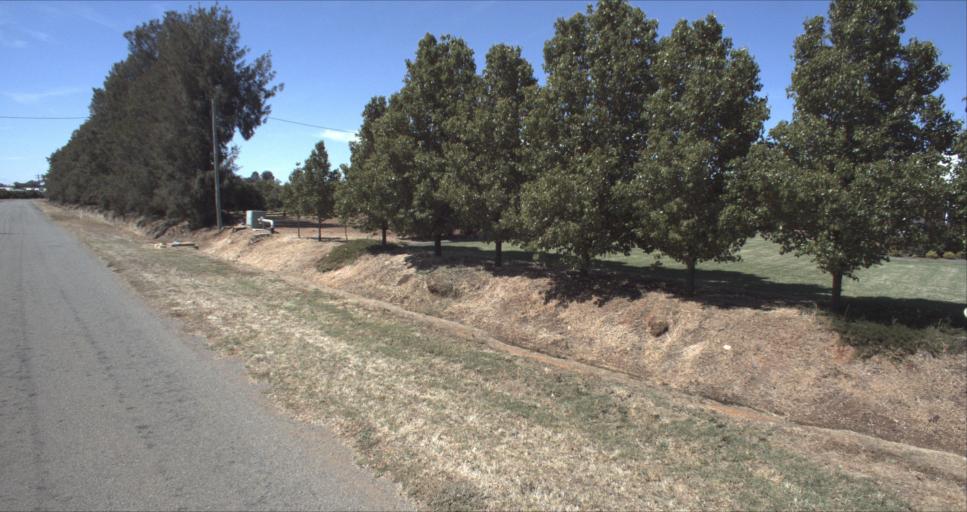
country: AU
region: New South Wales
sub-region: Leeton
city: Leeton
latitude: -34.6023
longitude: 146.4345
